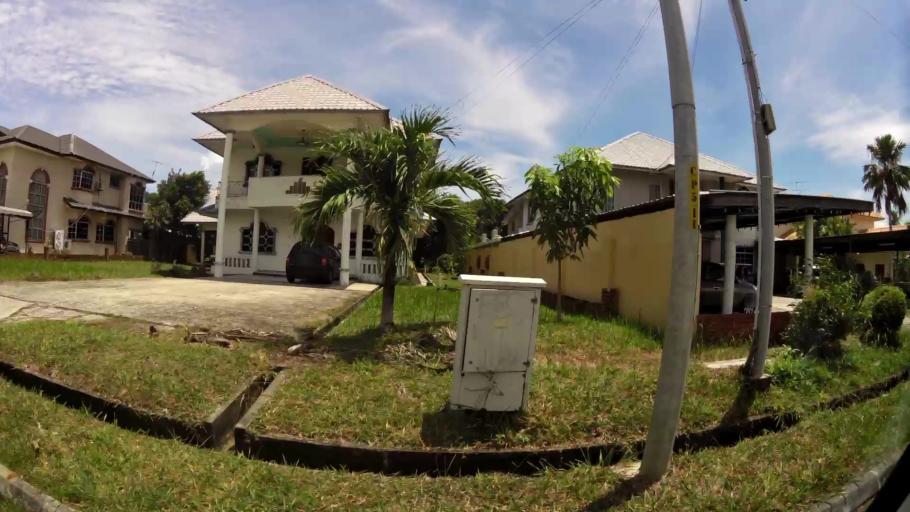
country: BN
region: Brunei and Muara
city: Bandar Seri Begawan
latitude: 4.9638
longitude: 114.9133
